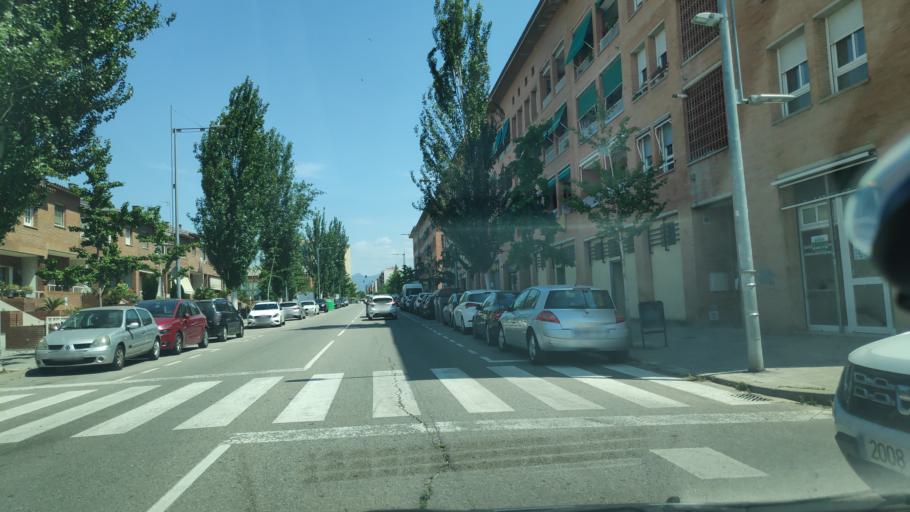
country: ES
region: Catalonia
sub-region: Provincia de Barcelona
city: Granollers
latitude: 41.5990
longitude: 2.2824
